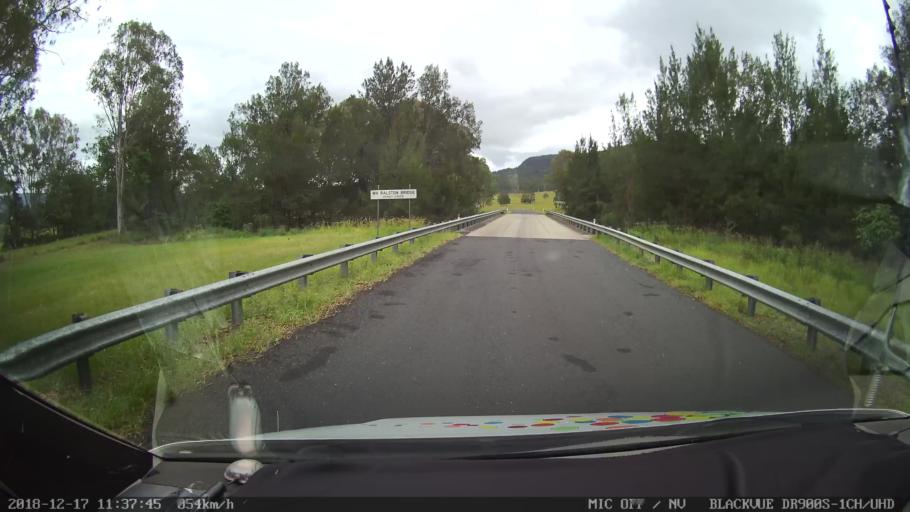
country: AU
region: New South Wales
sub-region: Kyogle
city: Kyogle
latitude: -28.7022
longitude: 152.6026
